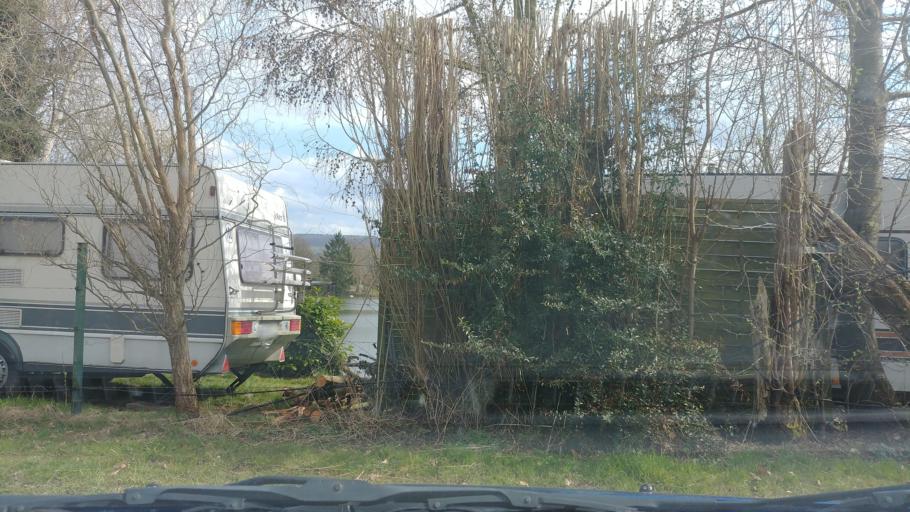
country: DE
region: Lower Saxony
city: Boffzen
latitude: 51.7485
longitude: 9.3723
